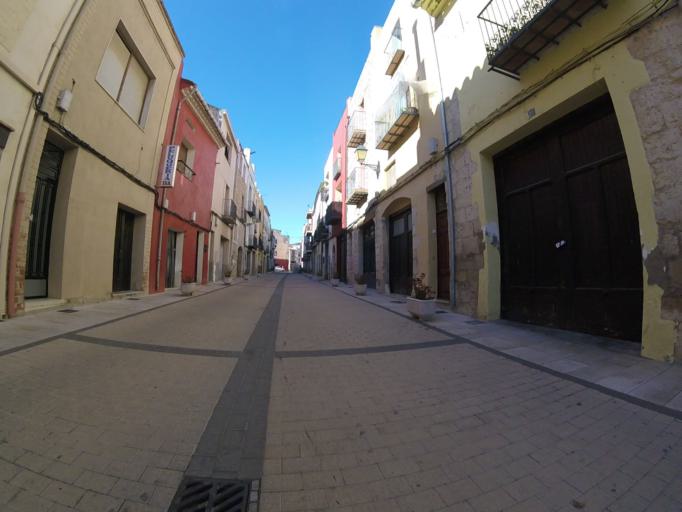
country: ES
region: Valencia
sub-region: Provincia de Castello
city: Chert/Xert
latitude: 40.4658
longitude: 0.1813
